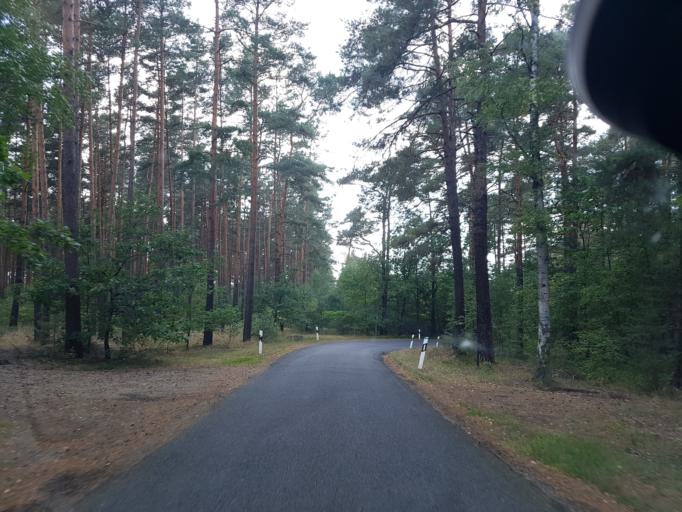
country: DE
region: Brandenburg
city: Bronkow
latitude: 51.7036
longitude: 13.9026
